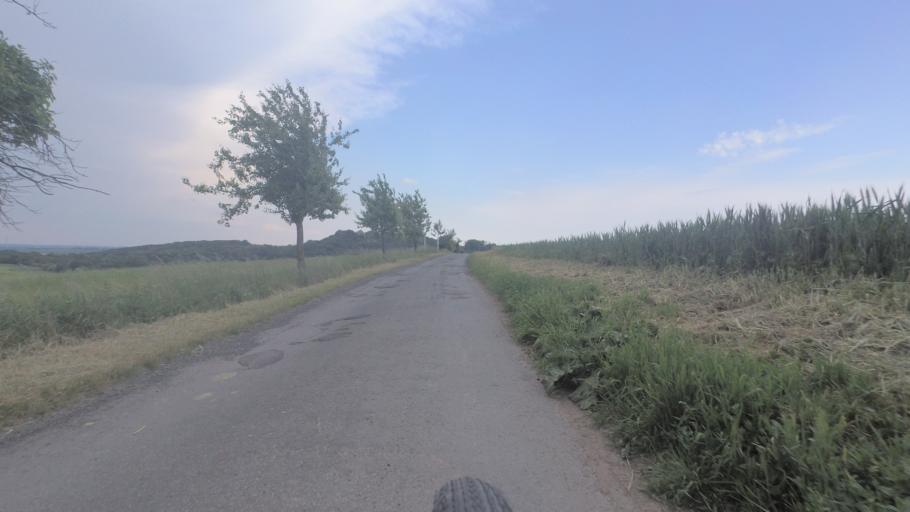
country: DE
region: Saxony-Anhalt
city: Hoym
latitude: 51.7135
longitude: 11.3386
